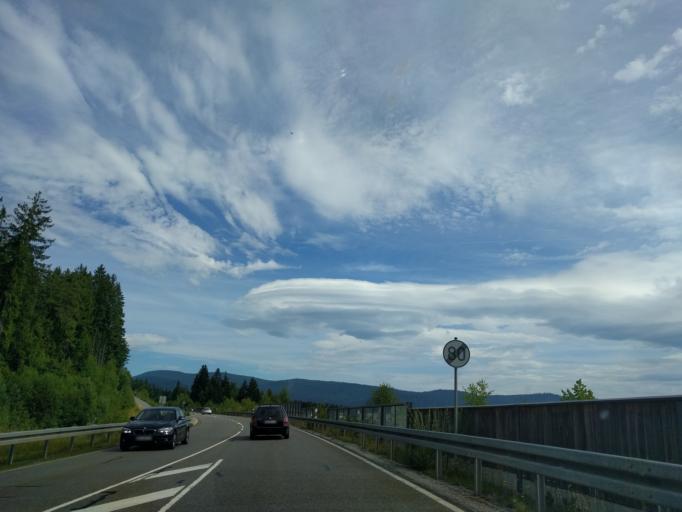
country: DE
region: Bavaria
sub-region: Lower Bavaria
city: Langdorf
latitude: 49.0079
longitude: 13.1431
